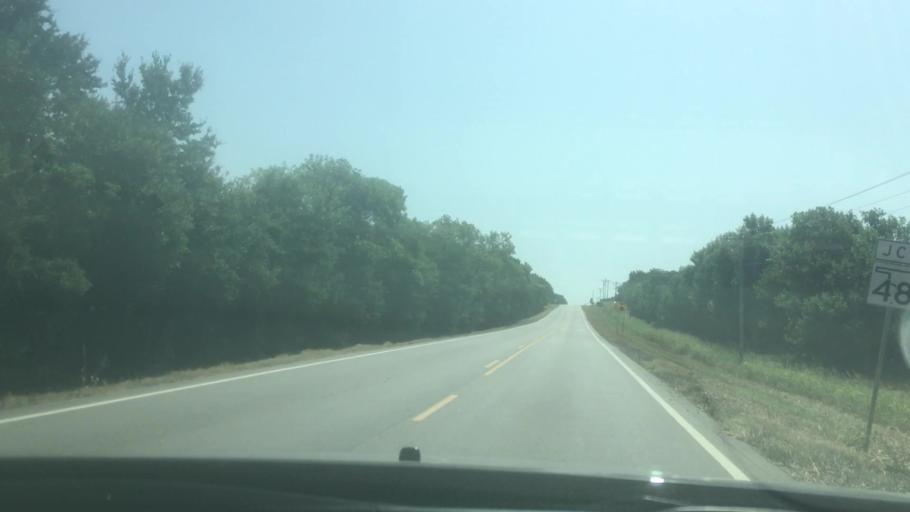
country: US
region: Oklahoma
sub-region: Bryan County
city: Durant
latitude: 34.1428
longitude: -96.3783
